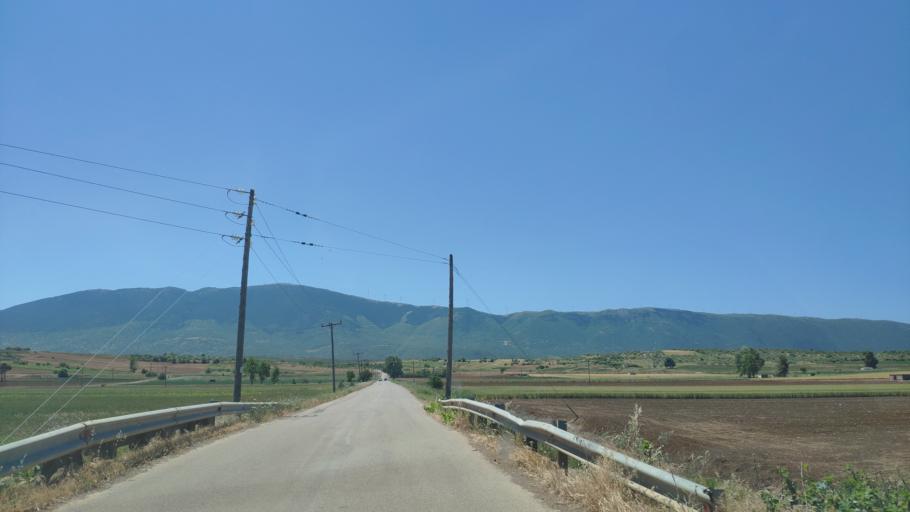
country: GR
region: Central Greece
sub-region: Nomos Voiotias
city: Kaparellion
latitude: 38.2594
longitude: 23.2352
